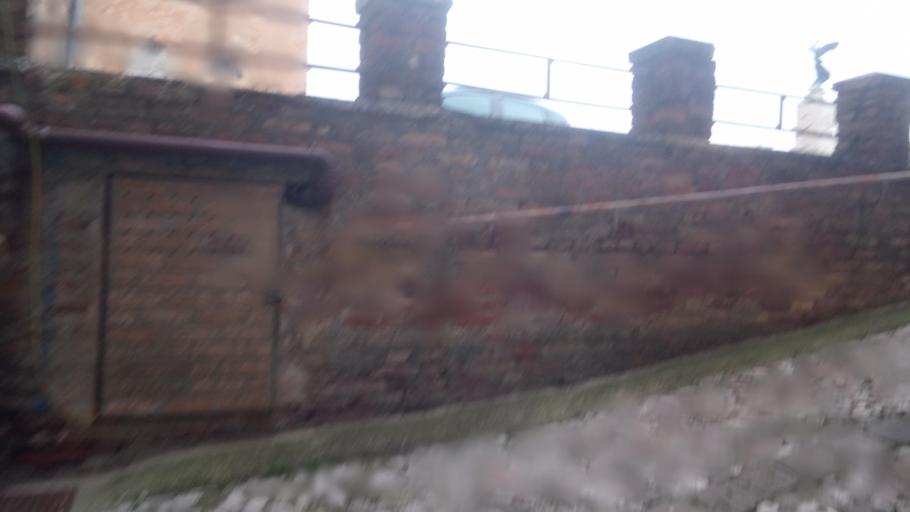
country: IT
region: The Marches
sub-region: Provincia di Ascoli Piceno
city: Ripatransone
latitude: 43.0009
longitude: 13.7631
